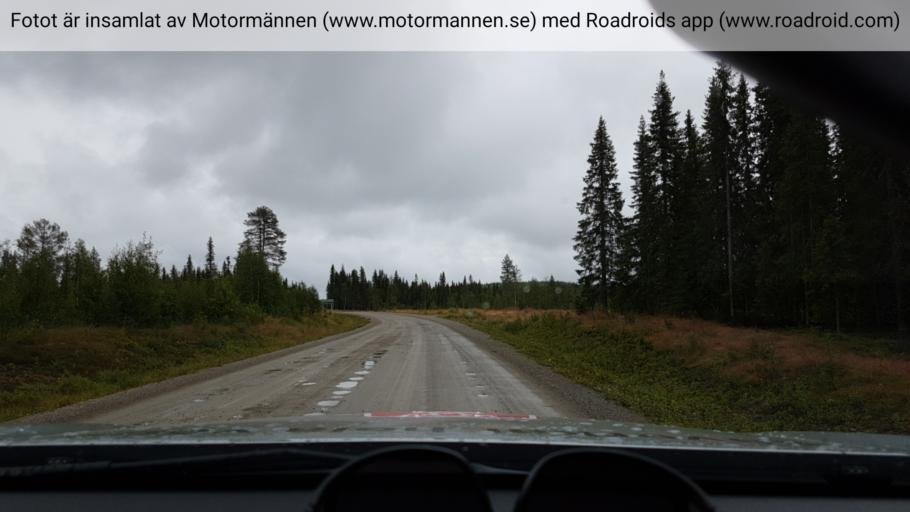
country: SE
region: Vaesterbotten
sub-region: Storumans Kommun
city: Storuman
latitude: 64.8539
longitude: 17.4003
